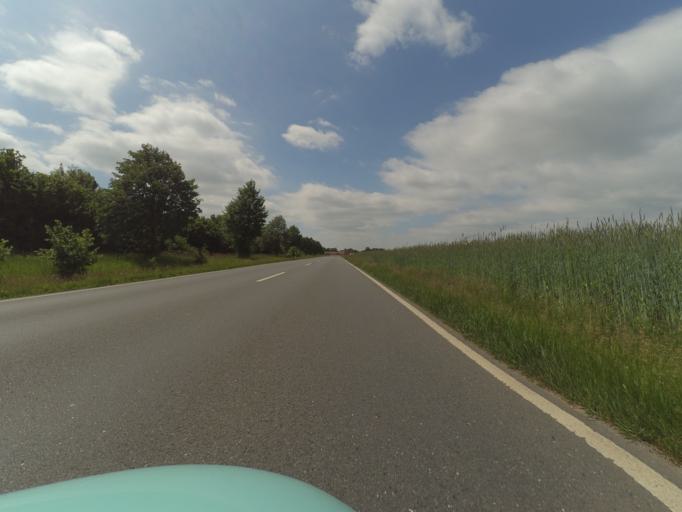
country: DE
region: Lower Saxony
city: Arpke
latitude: 52.3954
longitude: 10.0806
